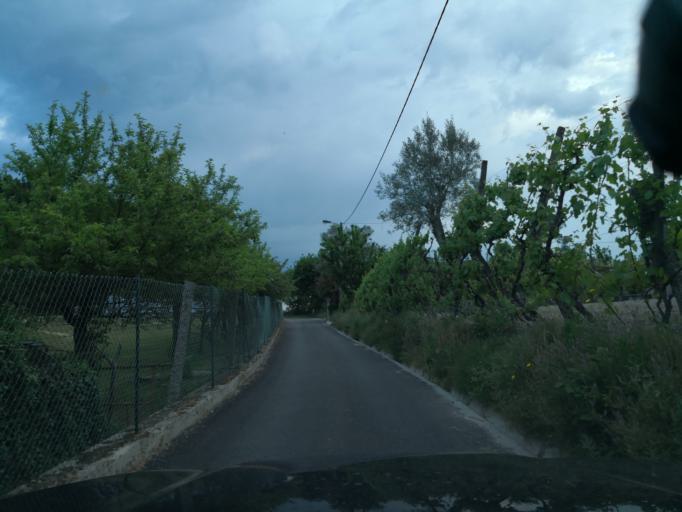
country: PT
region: Vila Real
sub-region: Vila Real
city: Vila Real
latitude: 41.3226
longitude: -7.7506
